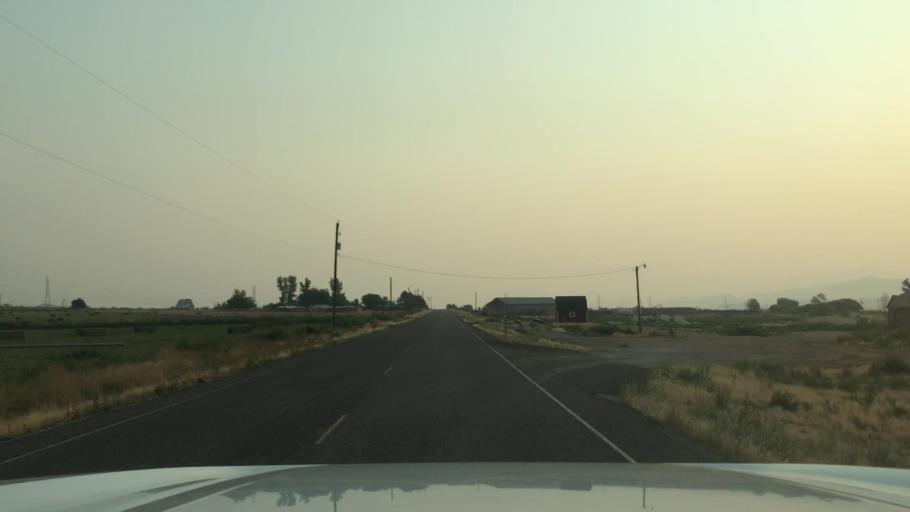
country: US
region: Utah
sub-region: Sevier County
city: Aurora
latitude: 38.8859
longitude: -111.9579
